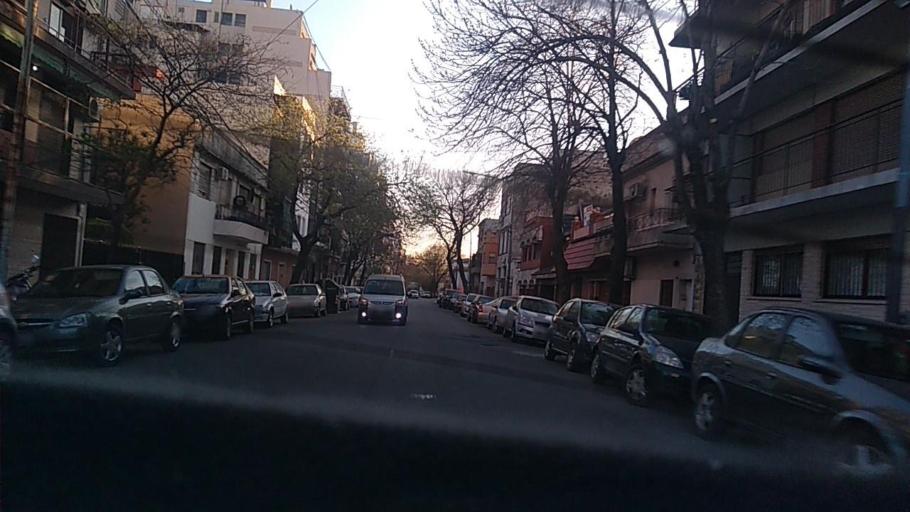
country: AR
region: Buenos Aires F.D.
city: Villa Santa Rita
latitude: -34.6063
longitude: -58.4841
